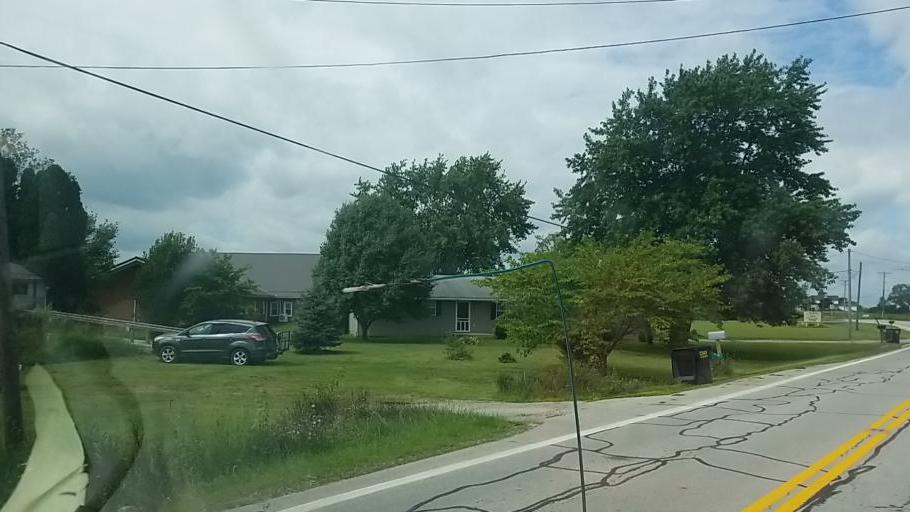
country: US
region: Ohio
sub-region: Fayette County
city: Jeffersonville
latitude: 39.6627
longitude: -83.5736
